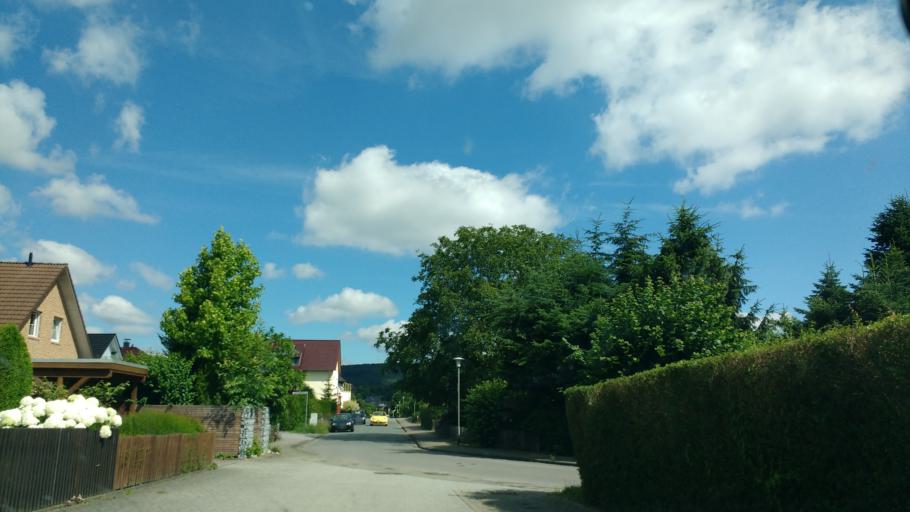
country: DE
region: Lower Saxony
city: Bad Pyrmont
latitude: 51.9811
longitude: 9.2270
